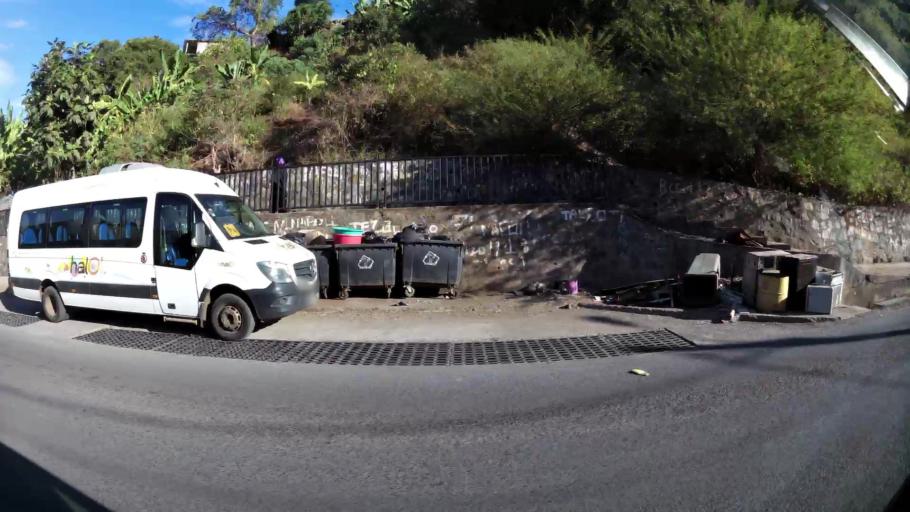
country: YT
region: Koungou
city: Koungou
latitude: -12.7451
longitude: 45.2201
